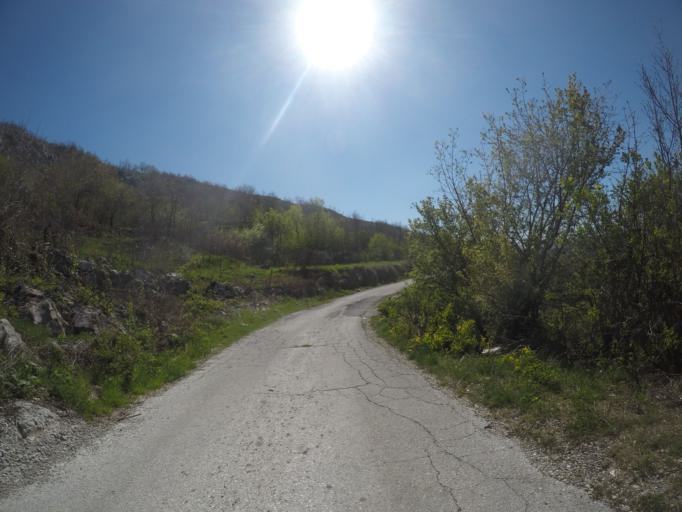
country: ME
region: Danilovgrad
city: Danilovgrad
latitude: 42.5359
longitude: 19.0155
